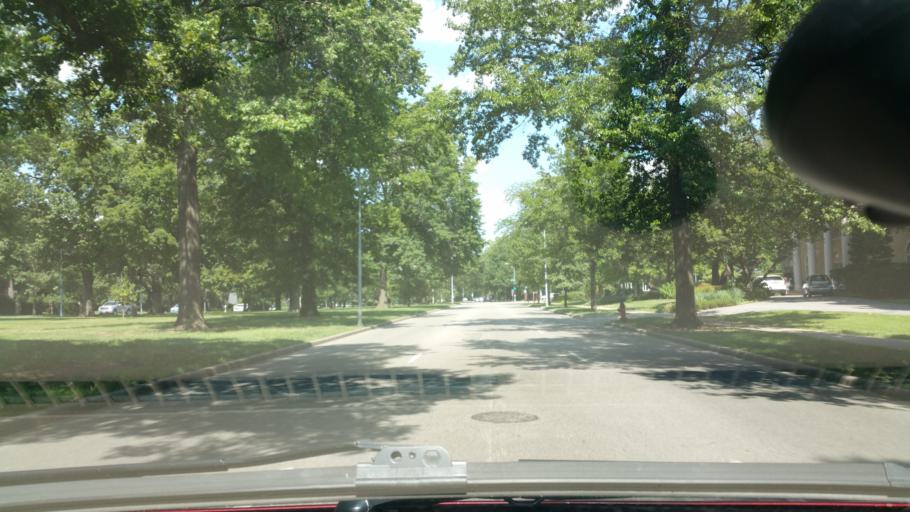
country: US
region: Kansas
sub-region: Johnson County
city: Mission Hills
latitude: 39.0194
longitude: -94.6016
